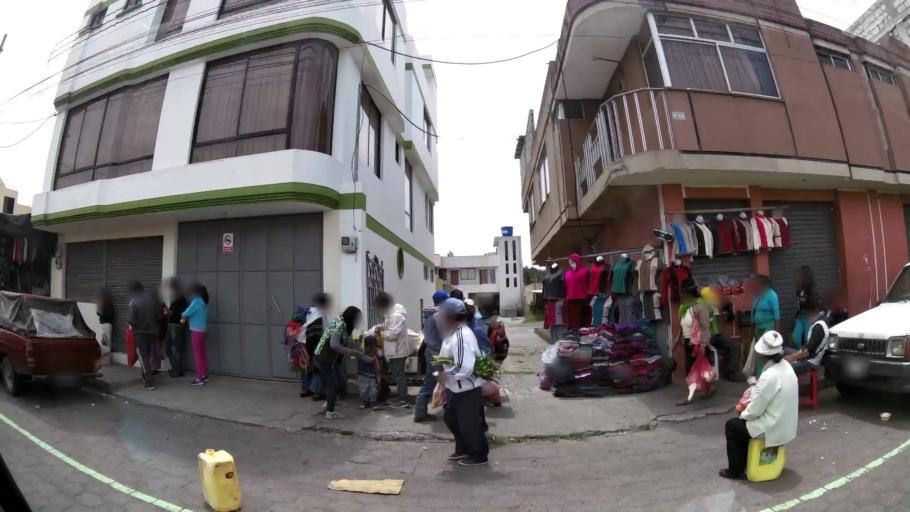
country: EC
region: Cotopaxi
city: San Miguel de Salcedo
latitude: -1.0458
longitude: -78.5920
